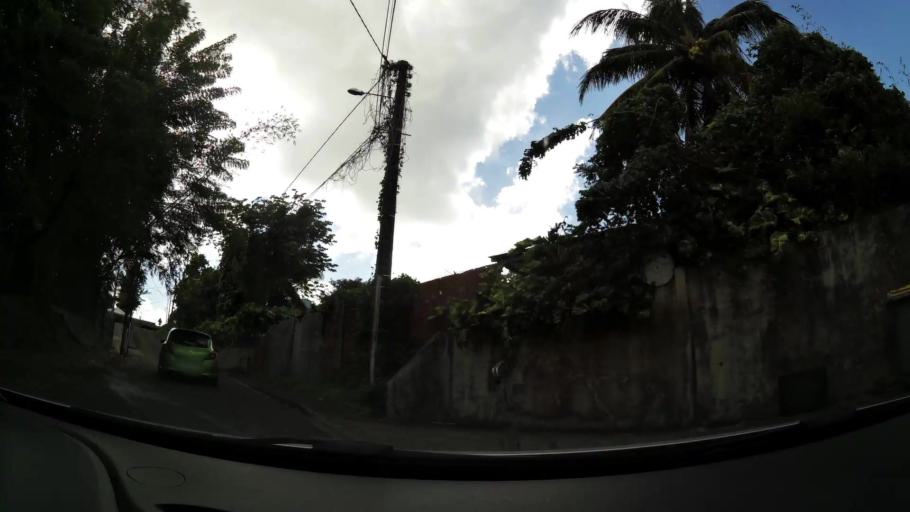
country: MQ
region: Martinique
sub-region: Martinique
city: Fort-de-France
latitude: 14.6332
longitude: -61.0534
